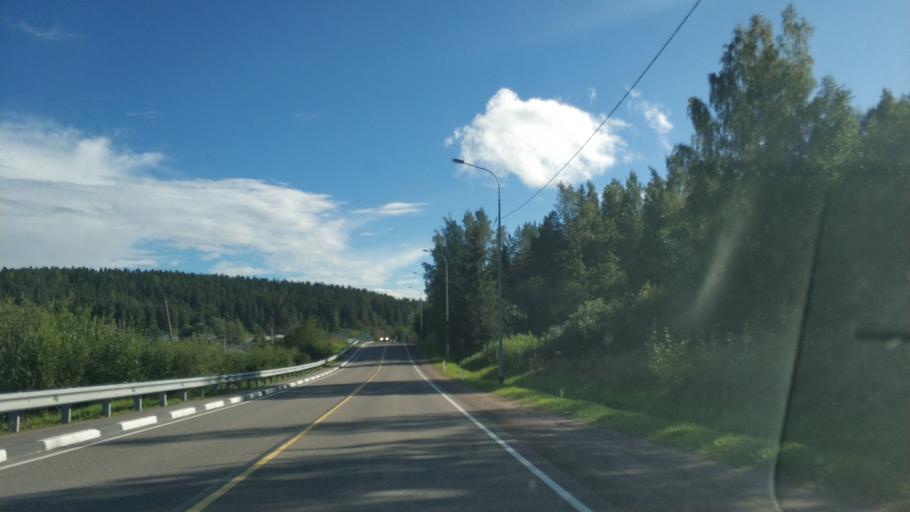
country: RU
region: Republic of Karelia
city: Sortavala
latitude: 61.6629
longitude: 30.6551
